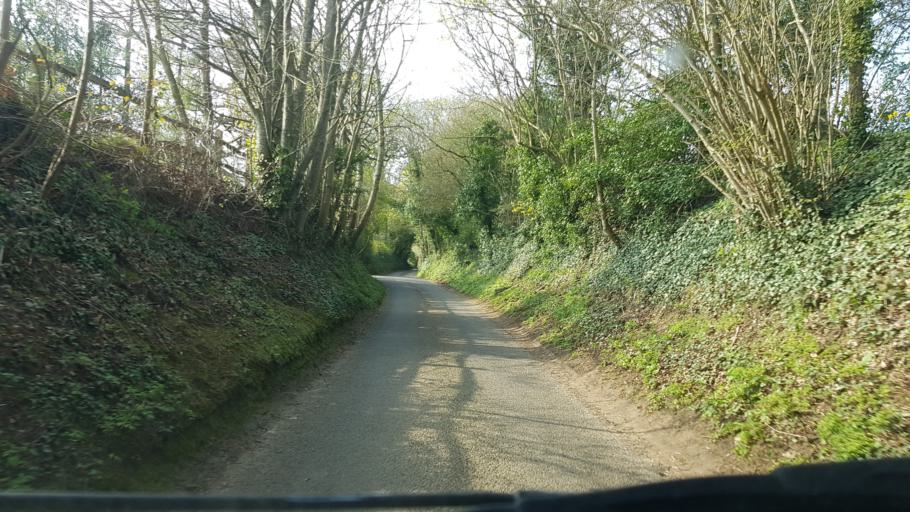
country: GB
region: England
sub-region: Surrey
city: Chilworth
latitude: 51.2225
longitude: -0.5053
